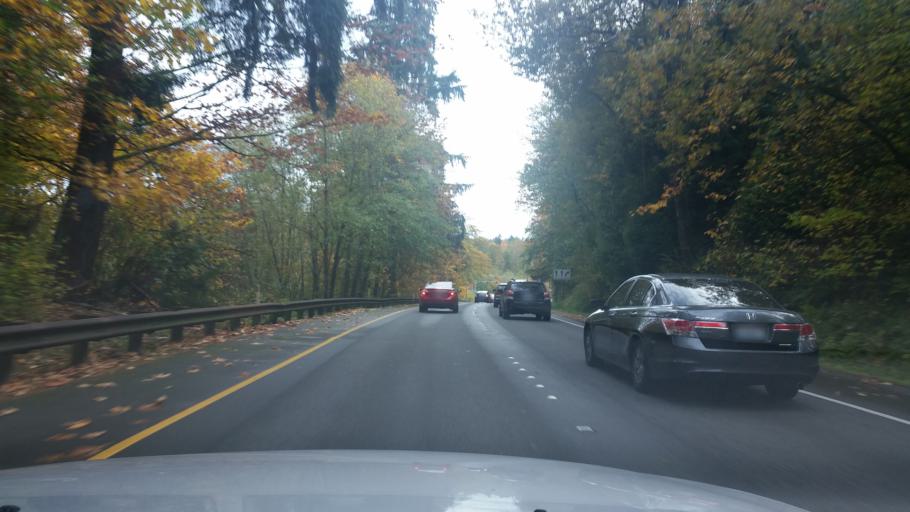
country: US
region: Washington
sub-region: King County
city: Newport
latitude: 47.5999
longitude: -122.1700
